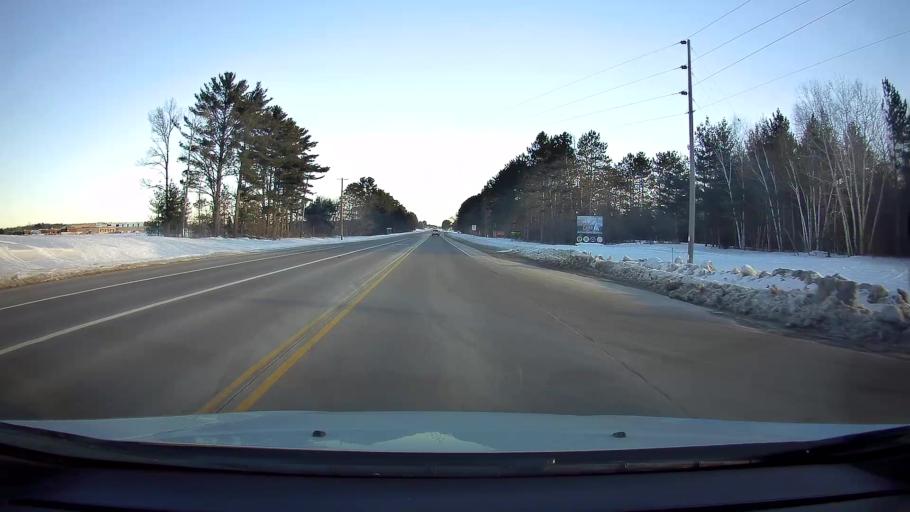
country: US
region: Wisconsin
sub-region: Washburn County
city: Shell Lake
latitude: 45.7251
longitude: -91.9348
